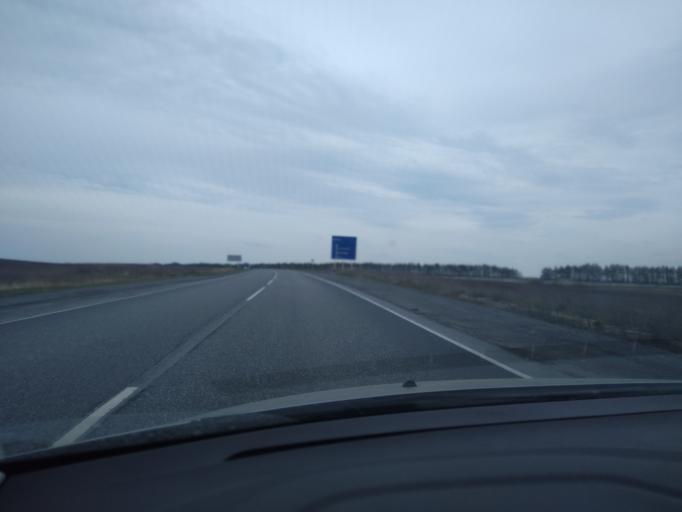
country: RU
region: Sverdlovsk
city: Kamyshlov
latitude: 56.8489
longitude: 62.8254
